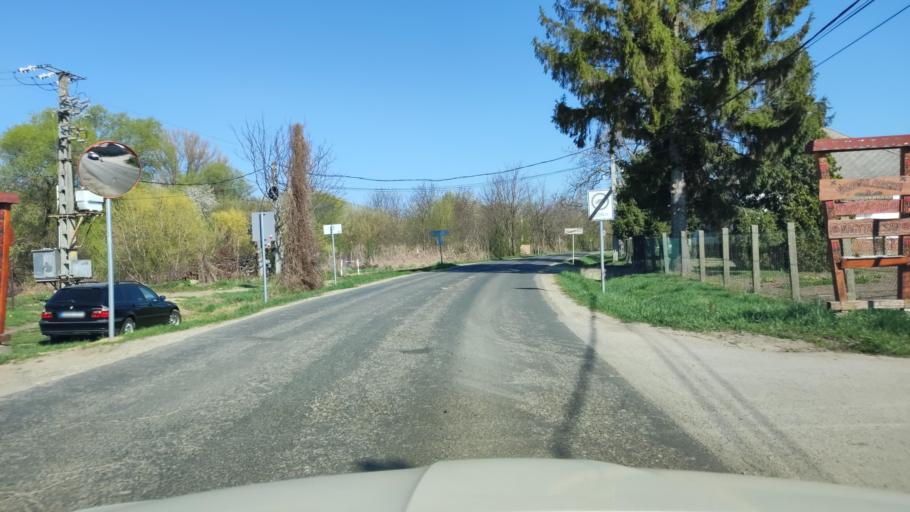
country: HU
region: Pest
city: Nagytarcsa
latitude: 47.5345
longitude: 19.2788
